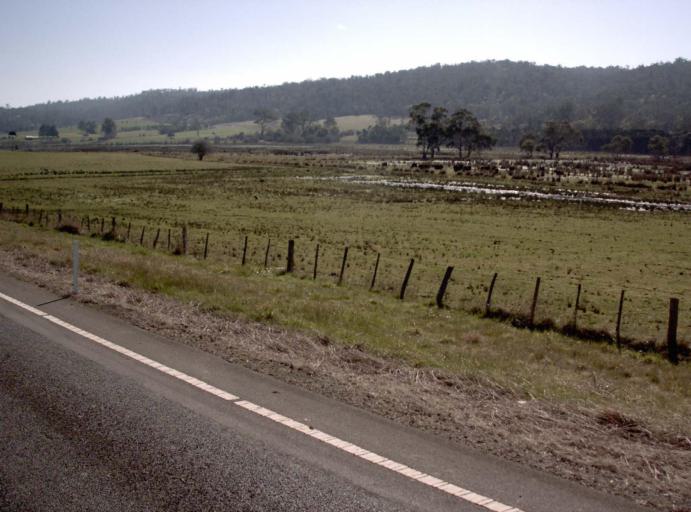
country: AU
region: Tasmania
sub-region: Launceston
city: Mayfield
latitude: -41.3237
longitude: 147.0628
